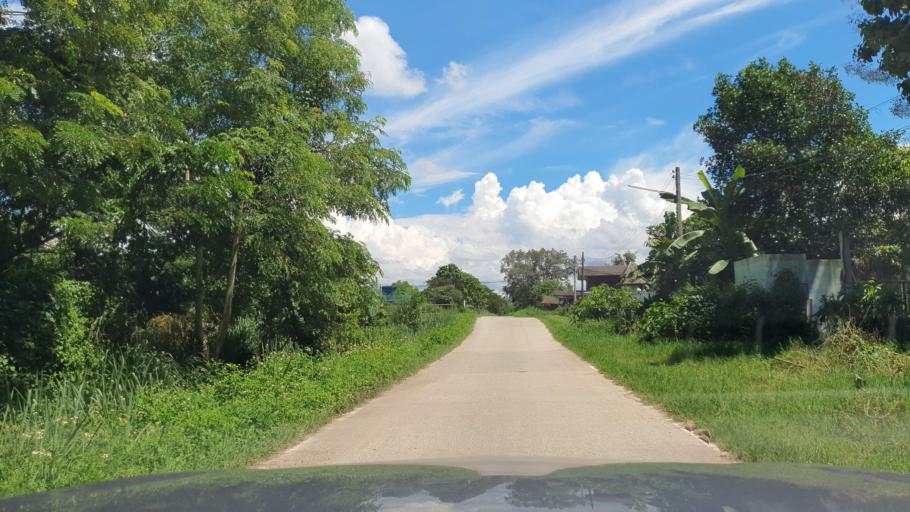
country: TH
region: Chiang Mai
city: San Kamphaeng
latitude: 18.7341
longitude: 99.1156
